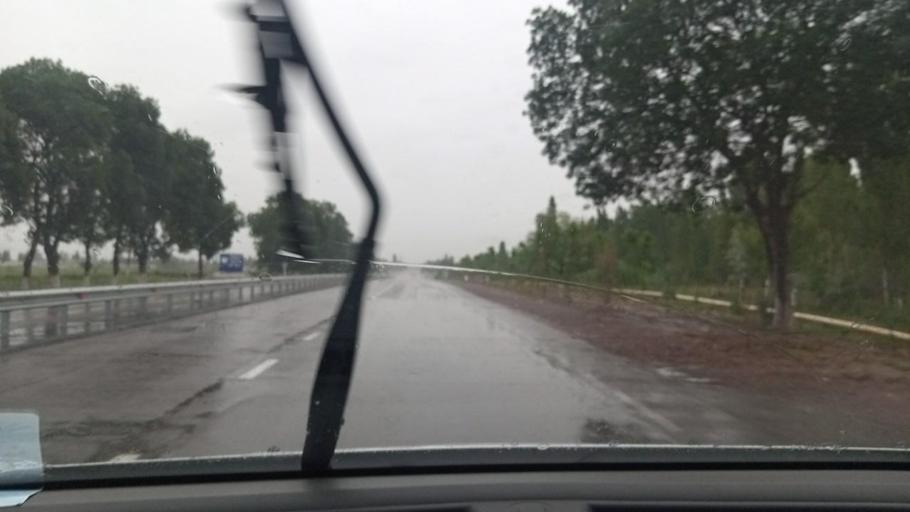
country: UZ
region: Toshkent
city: Angren
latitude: 40.9816
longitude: 70.0195
